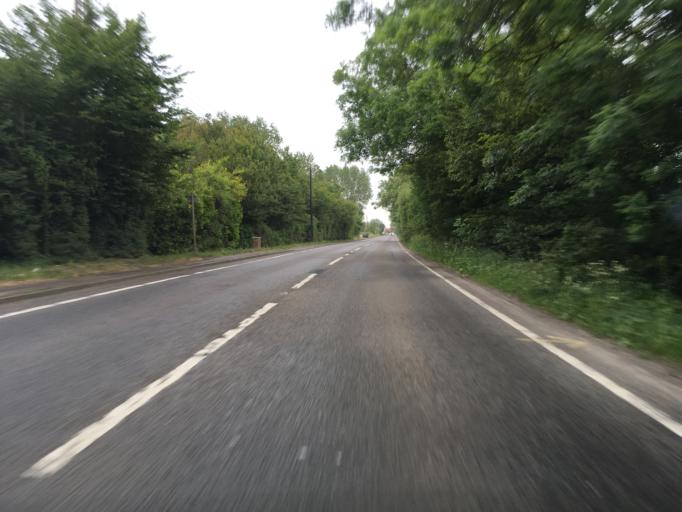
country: GB
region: England
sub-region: North Somerset
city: St. Georges
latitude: 51.3633
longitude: -2.8799
